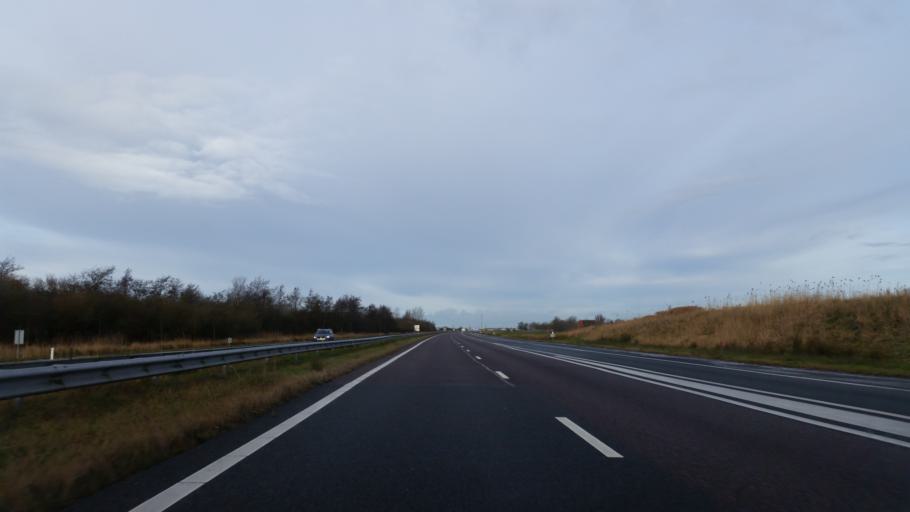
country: NL
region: Friesland
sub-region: Gemeente Boarnsterhim
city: Reduzum
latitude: 53.1153
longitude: 5.8113
